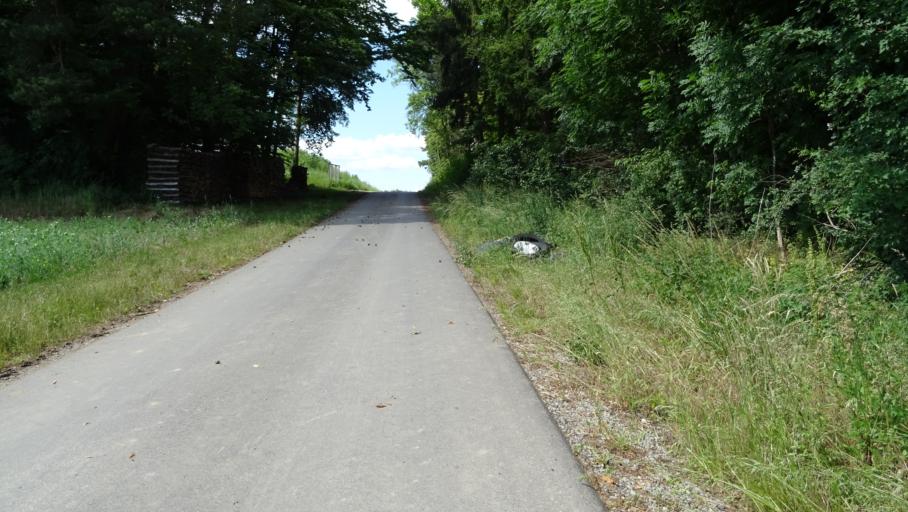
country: DE
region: Baden-Wuerttemberg
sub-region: Karlsruhe Region
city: Adelsheim
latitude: 49.4095
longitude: 9.3658
